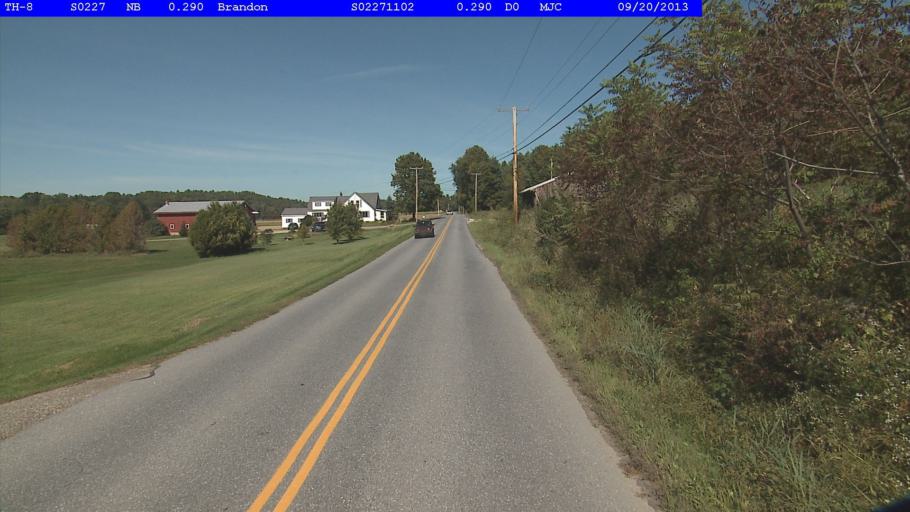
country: US
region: Vermont
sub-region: Rutland County
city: Brandon
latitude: 43.7786
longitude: -73.0522
